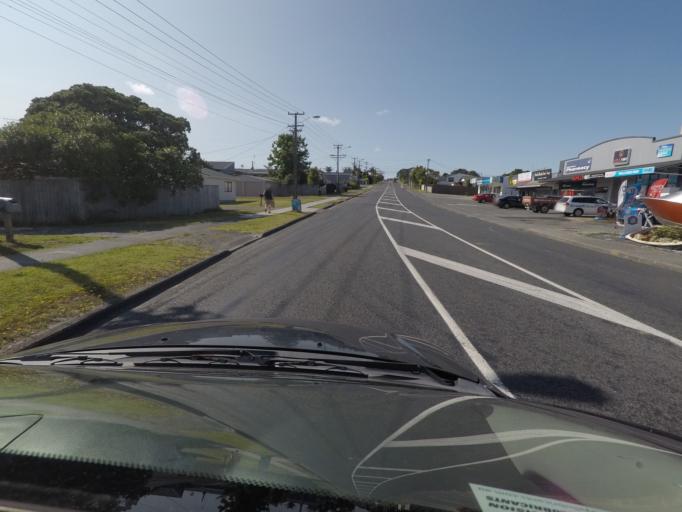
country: NZ
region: Auckland
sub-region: Auckland
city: Warkworth
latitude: -36.4233
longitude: 174.7268
